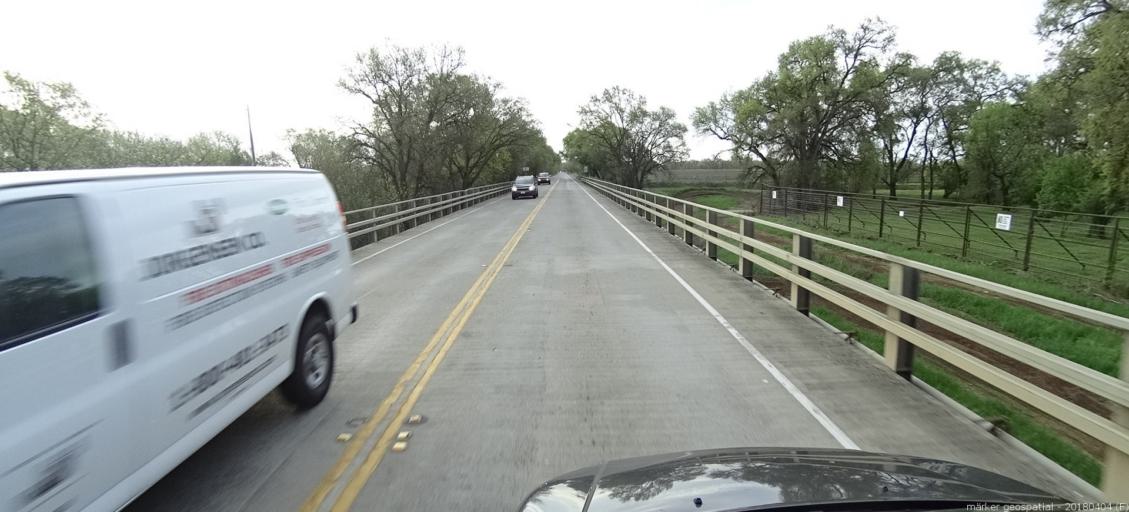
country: US
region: California
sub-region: Sacramento County
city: Wilton
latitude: 38.4212
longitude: -121.2865
